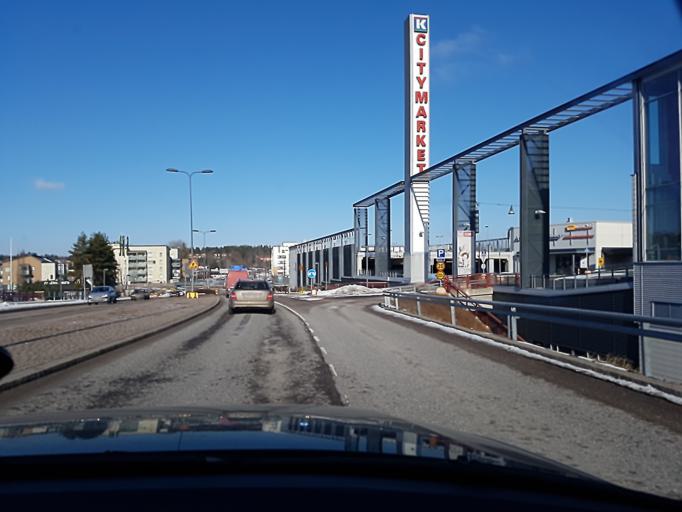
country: FI
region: Uusimaa
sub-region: Helsinki
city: Kirkkonummi
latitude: 60.1202
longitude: 24.4427
